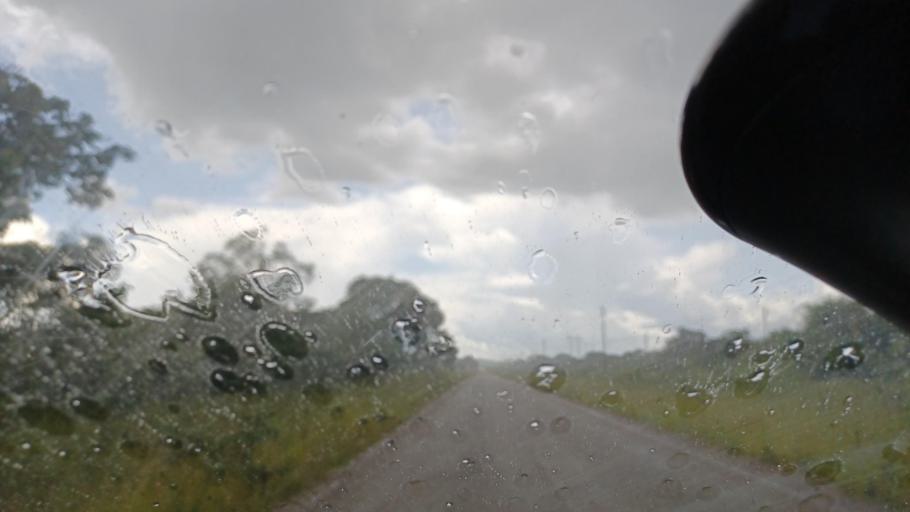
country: ZM
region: North-Western
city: Kasempa
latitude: -13.0993
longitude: 25.8998
